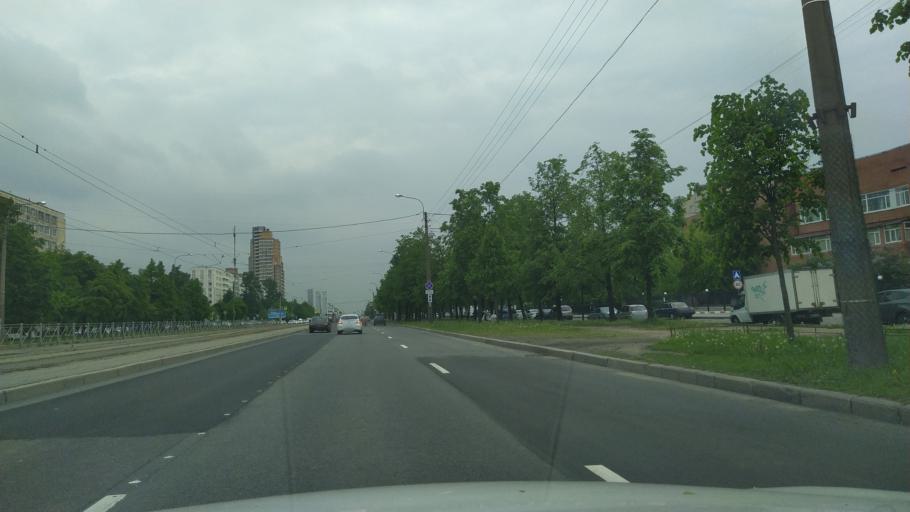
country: RU
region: St.-Petersburg
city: Kupchino
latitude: 59.8644
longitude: 30.3868
